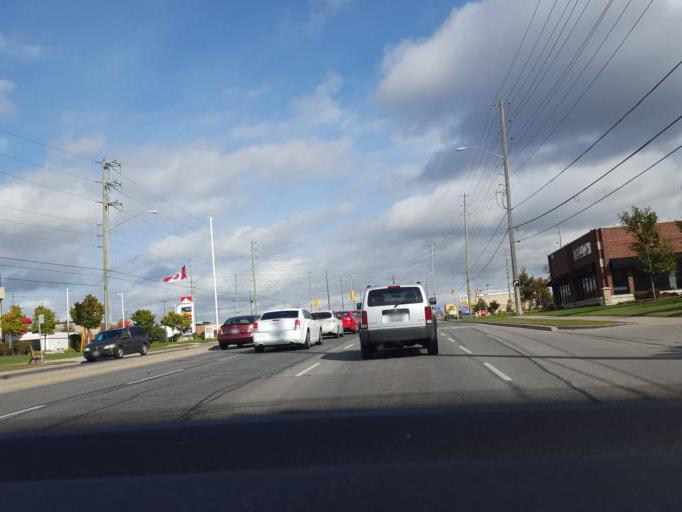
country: CA
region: Ontario
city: Oshawa
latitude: 43.9391
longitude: -78.8511
